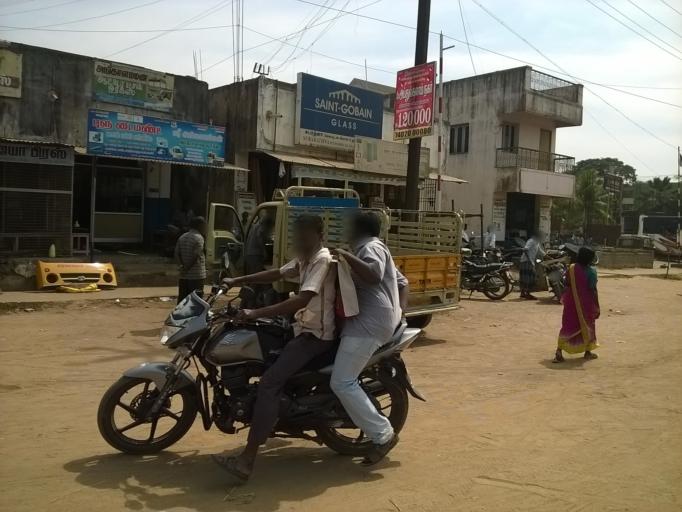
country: IN
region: Tamil Nadu
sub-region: Cuddalore
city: Panruti
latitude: 11.7668
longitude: 79.5497
